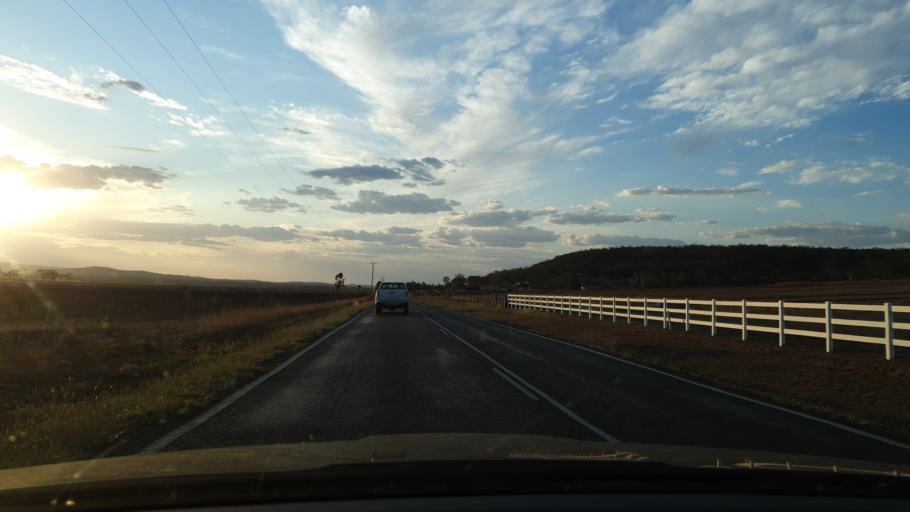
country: AU
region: Queensland
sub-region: Southern Downs
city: Warwick
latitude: -28.1860
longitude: 152.0075
